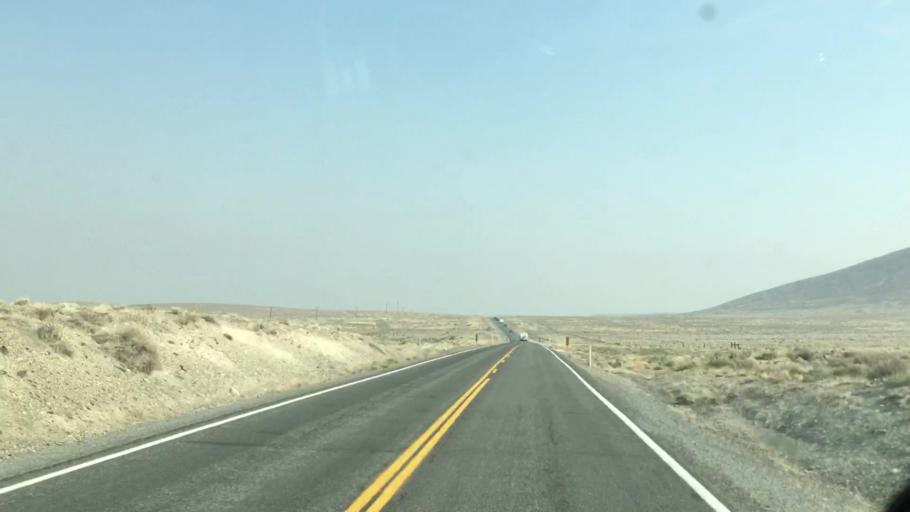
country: US
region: Nevada
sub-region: Lyon County
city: Fernley
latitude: 40.4999
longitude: -119.3347
